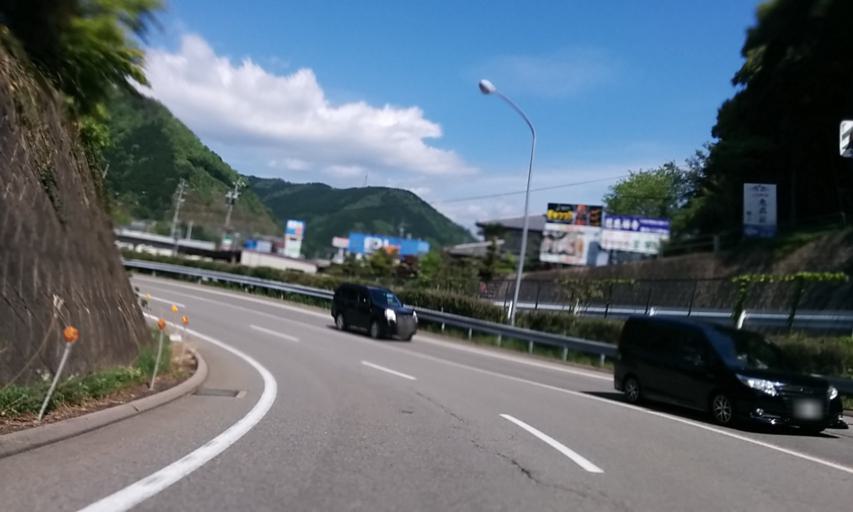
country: JP
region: Gifu
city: Gujo
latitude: 35.7522
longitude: 136.9472
